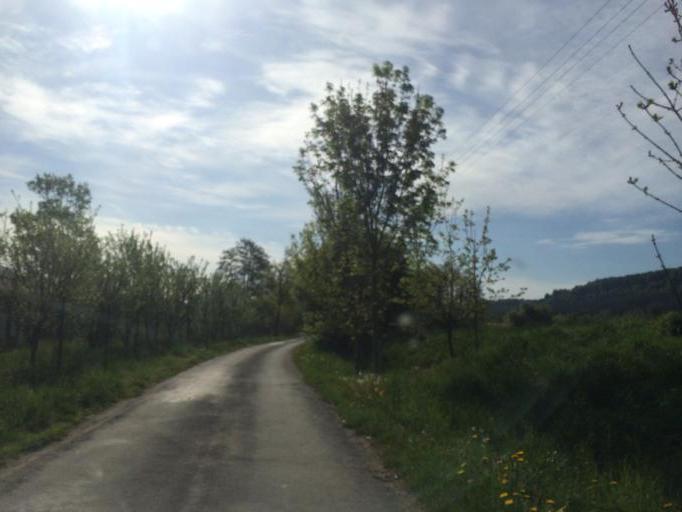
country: CZ
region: Central Bohemia
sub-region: Okres Mlada Boleslav
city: Zd'ar
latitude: 50.5456
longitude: 15.0505
